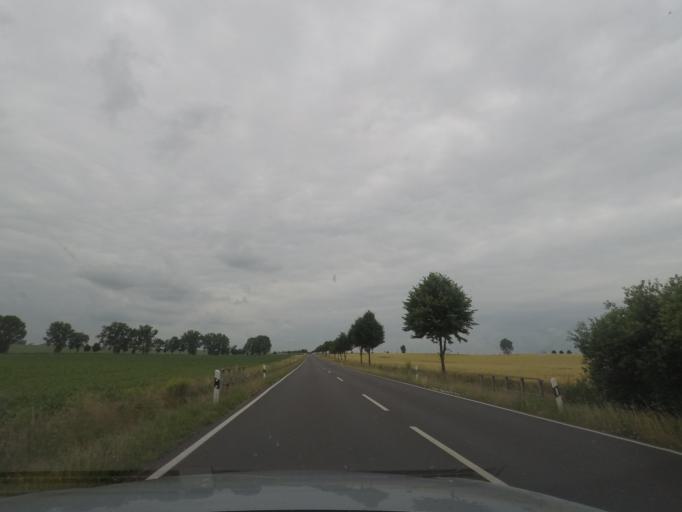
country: DE
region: Saxony-Anhalt
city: Erxleben
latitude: 52.2108
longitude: 11.2890
